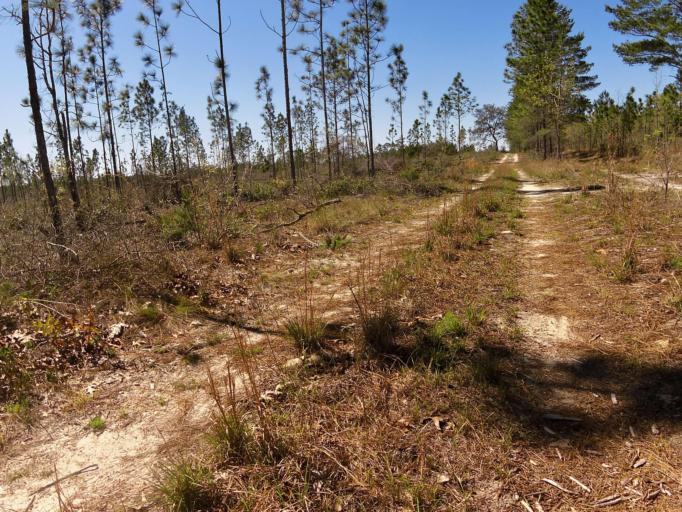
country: US
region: Florida
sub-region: Clay County
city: Keystone Heights
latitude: 29.8377
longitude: -81.9811
